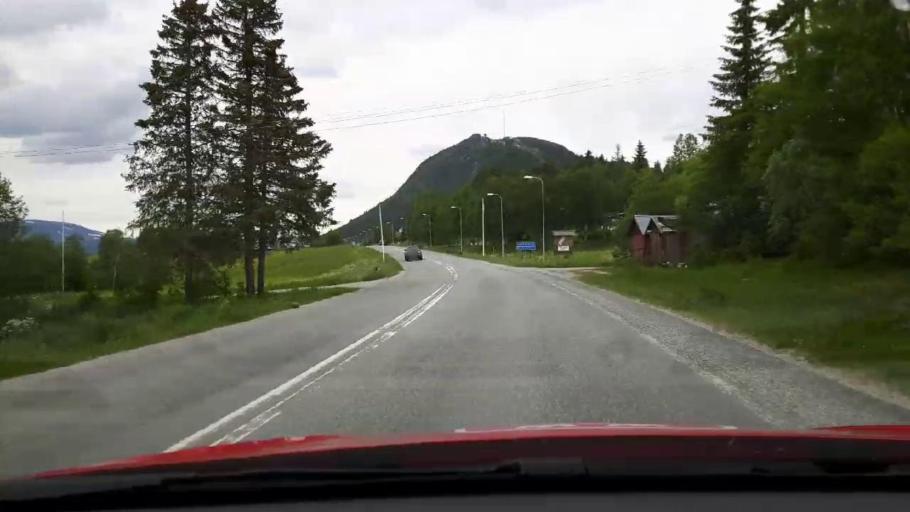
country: NO
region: Hedmark
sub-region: Engerdal
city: Engerdal
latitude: 62.5361
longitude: 12.5574
